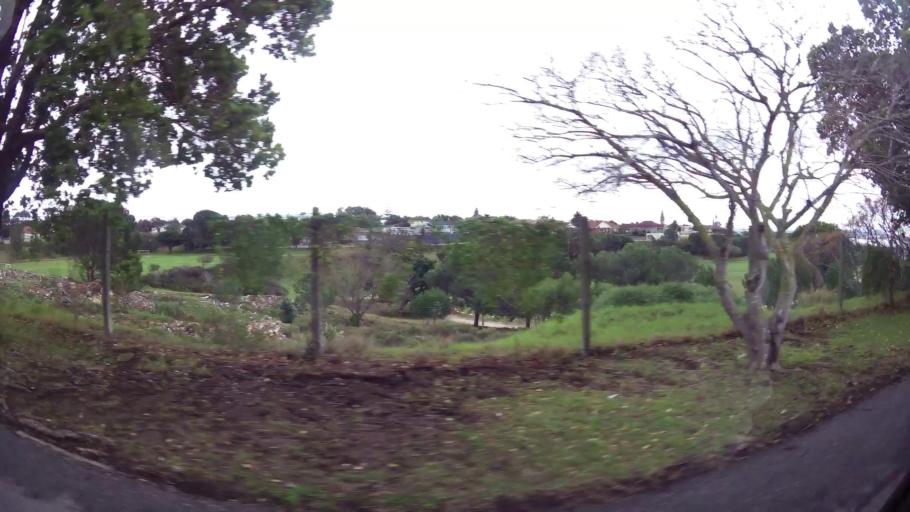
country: ZA
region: Eastern Cape
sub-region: Nelson Mandela Bay Metropolitan Municipality
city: Port Elizabeth
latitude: -33.9501
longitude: 25.5943
